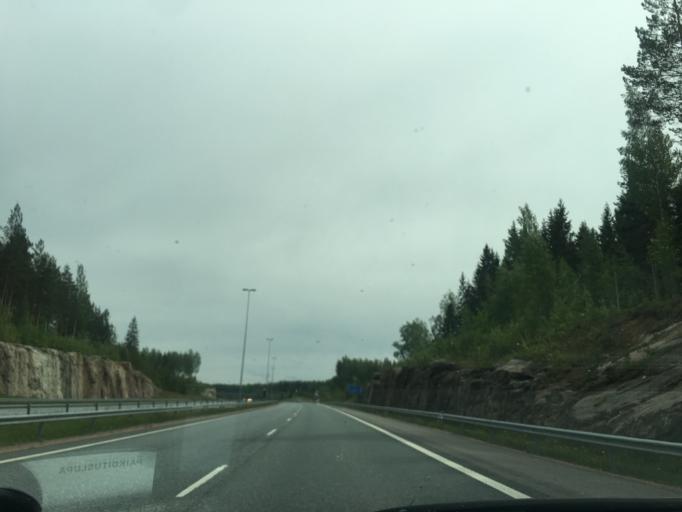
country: FI
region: Uusimaa
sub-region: Helsinki
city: Sammatti
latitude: 60.3467
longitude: 23.9029
